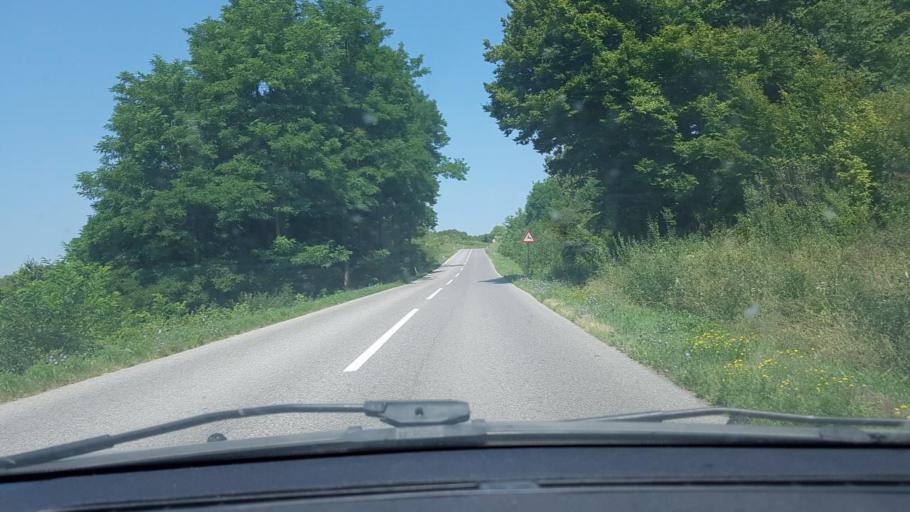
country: BA
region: Federation of Bosnia and Herzegovina
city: Velika Kladusa
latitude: 45.2042
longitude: 15.7741
